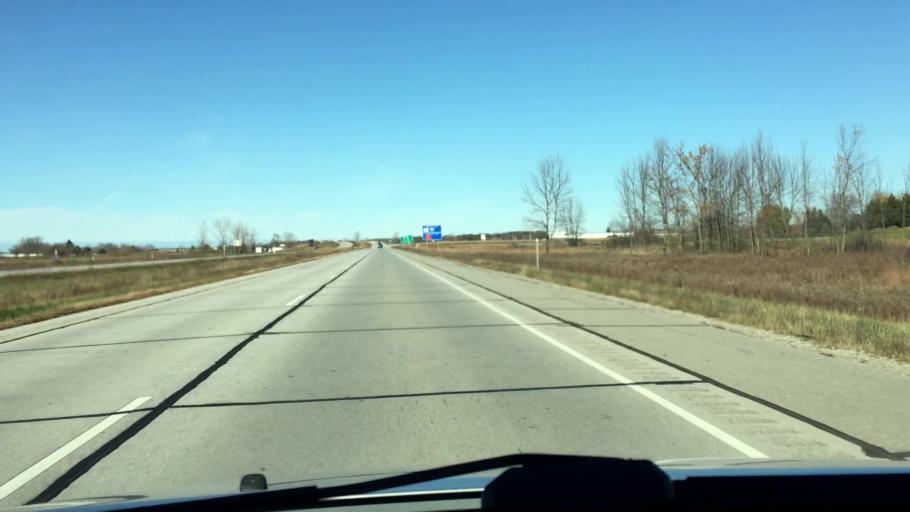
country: US
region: Wisconsin
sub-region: Brown County
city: Pulaski
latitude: 44.5926
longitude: -88.2084
